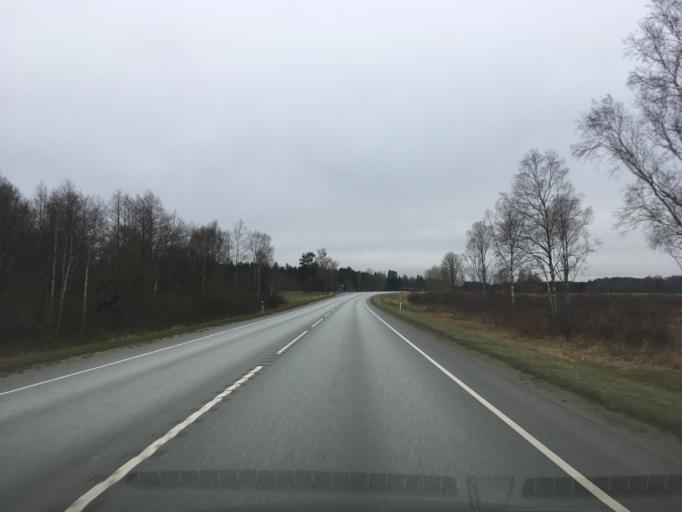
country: EE
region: Laeaene-Virumaa
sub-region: Viru-Nigula vald
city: Kunda
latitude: 59.4153
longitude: 26.6524
